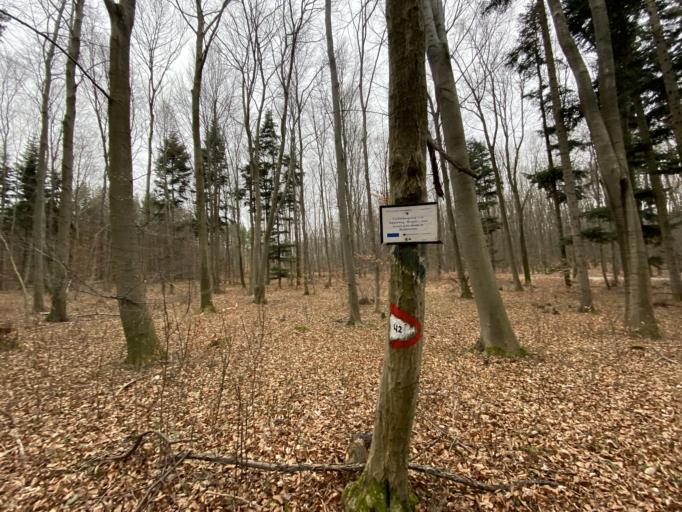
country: AT
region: Lower Austria
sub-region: Politischer Bezirk Modling
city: Gaaden
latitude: 48.0218
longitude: 16.2014
